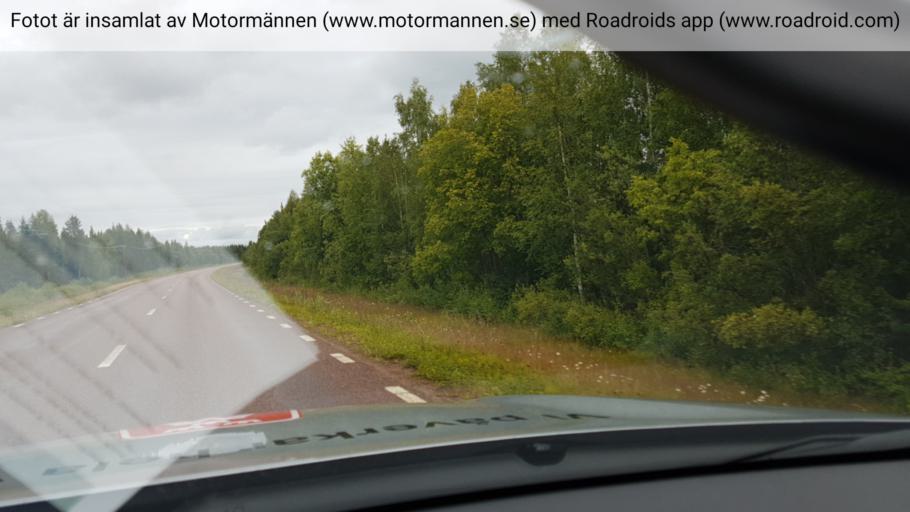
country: SE
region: Norrbotten
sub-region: Pajala Kommun
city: Pajala
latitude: 67.1277
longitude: 22.6058
